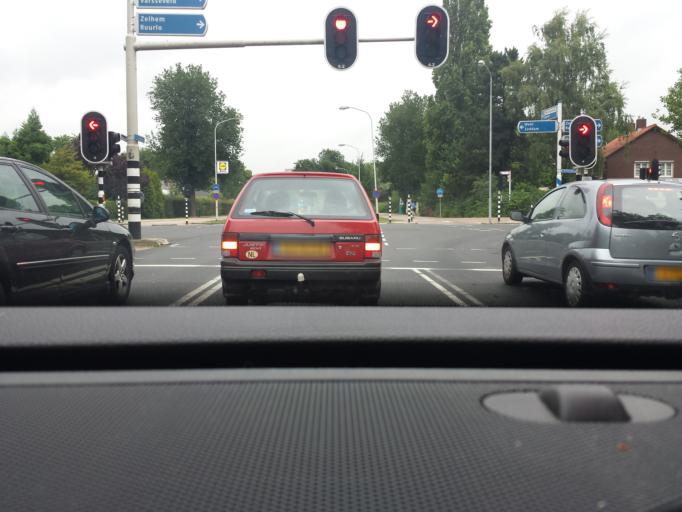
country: NL
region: Gelderland
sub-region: Gemeente Doetinchem
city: Doetinchem
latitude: 51.9659
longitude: 6.3015
